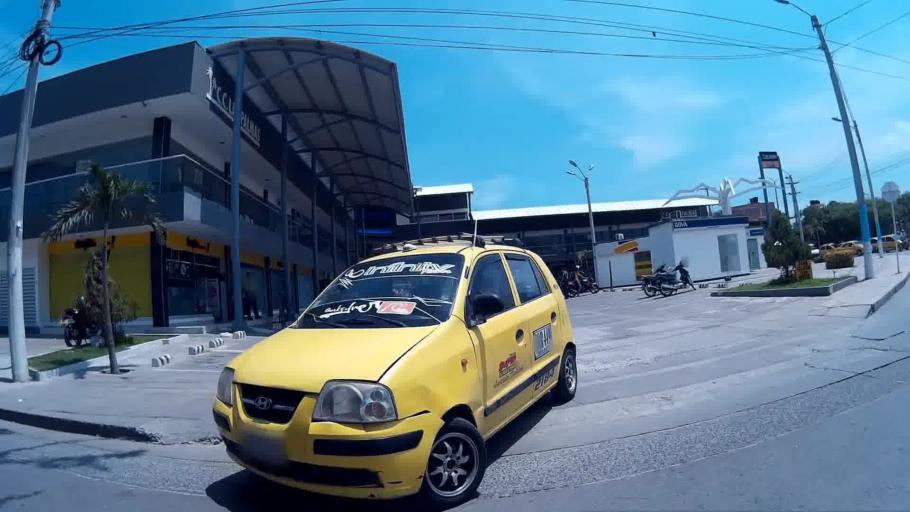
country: CO
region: Magdalena
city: Santa Marta
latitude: 11.2263
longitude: -74.1968
